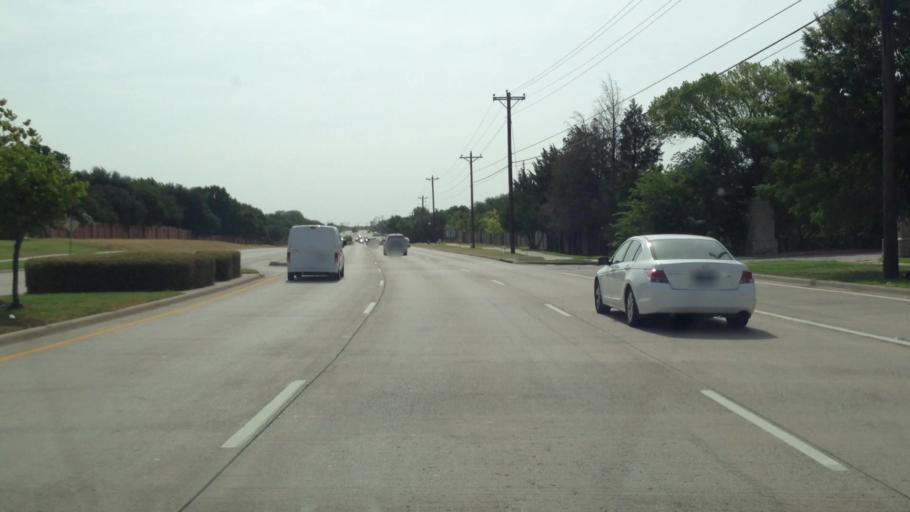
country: US
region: Texas
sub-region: Denton County
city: Flower Mound
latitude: 33.0100
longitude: -97.0435
